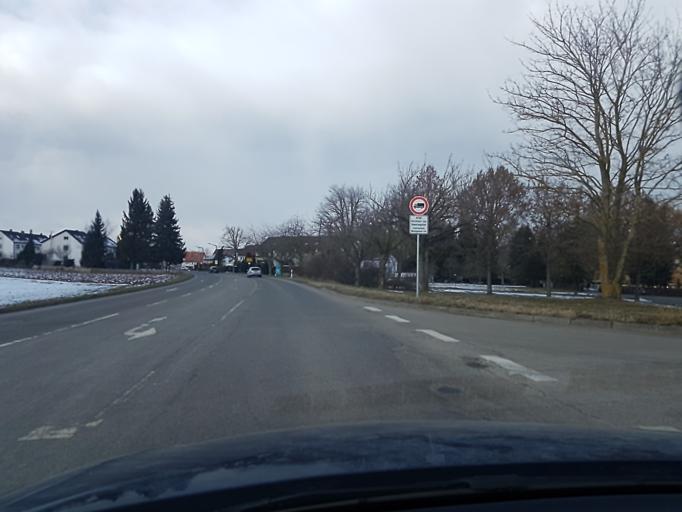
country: DE
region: Baden-Wuerttemberg
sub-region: Regierungsbezirk Stuttgart
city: Renningen
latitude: 48.7607
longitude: 8.9401
